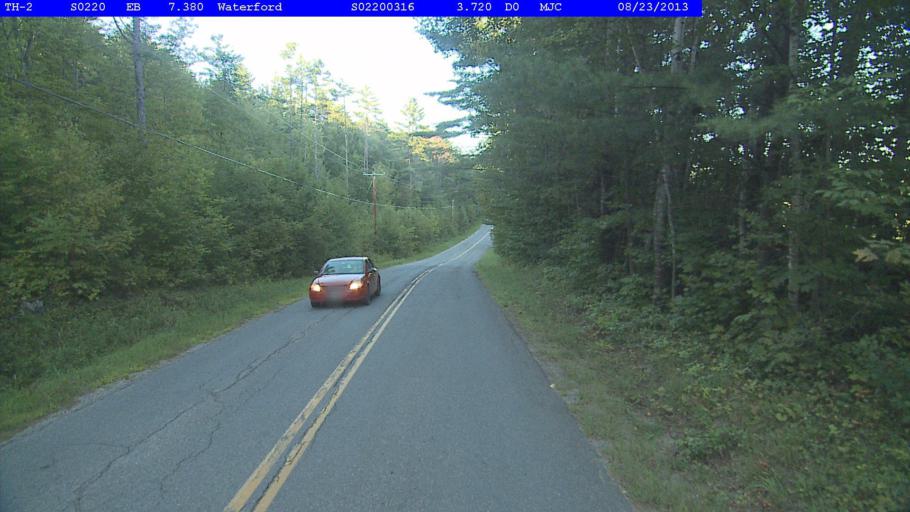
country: US
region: Vermont
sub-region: Caledonia County
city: Saint Johnsbury
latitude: 44.3439
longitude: -71.9310
